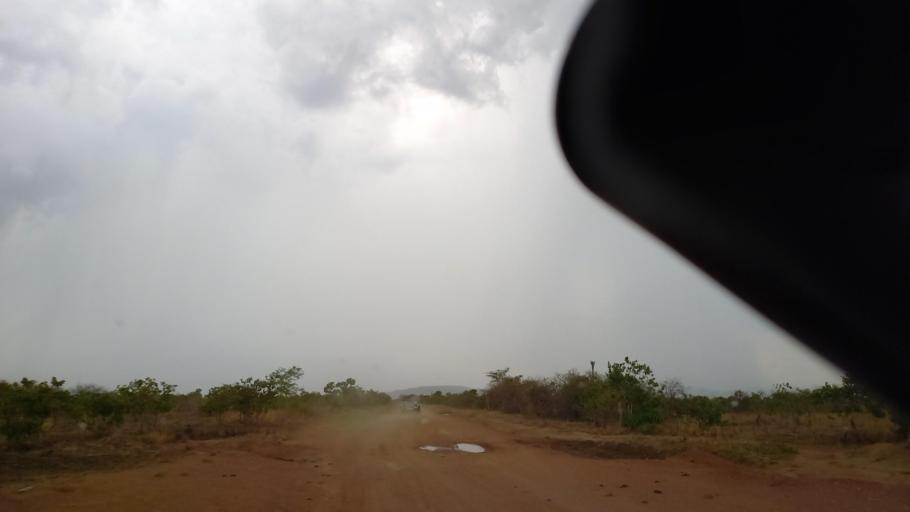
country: ZM
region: Lusaka
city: Kafue
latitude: -15.8688
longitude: 28.1955
